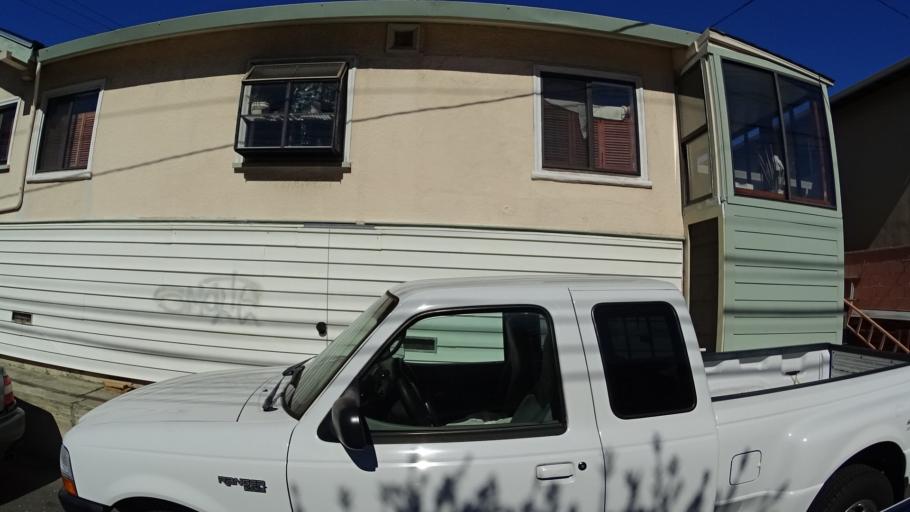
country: US
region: California
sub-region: San Mateo County
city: South San Francisco
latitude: 37.6533
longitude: -122.4130
